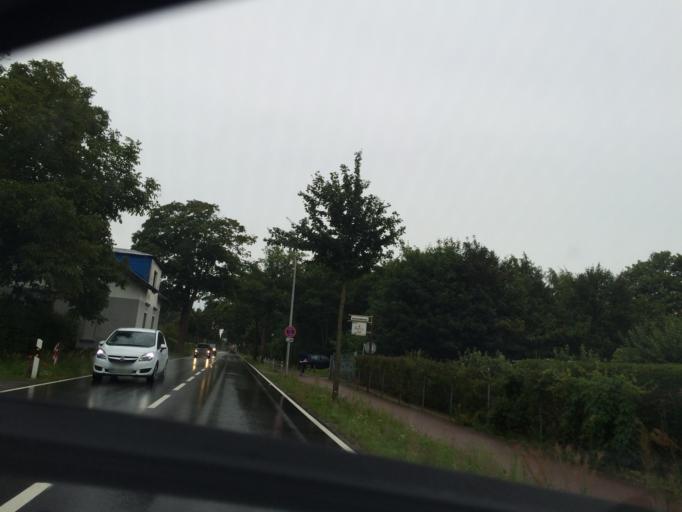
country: DE
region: Mecklenburg-Vorpommern
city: Kramerhof
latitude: 54.3355
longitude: 13.0615
